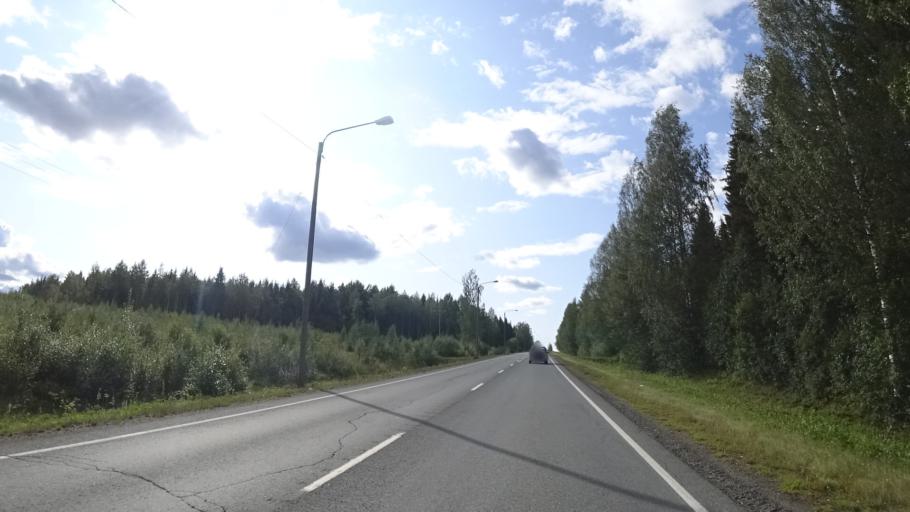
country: FI
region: North Karelia
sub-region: Keski-Karjala
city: Tohmajaervi
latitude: 62.2217
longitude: 30.3681
